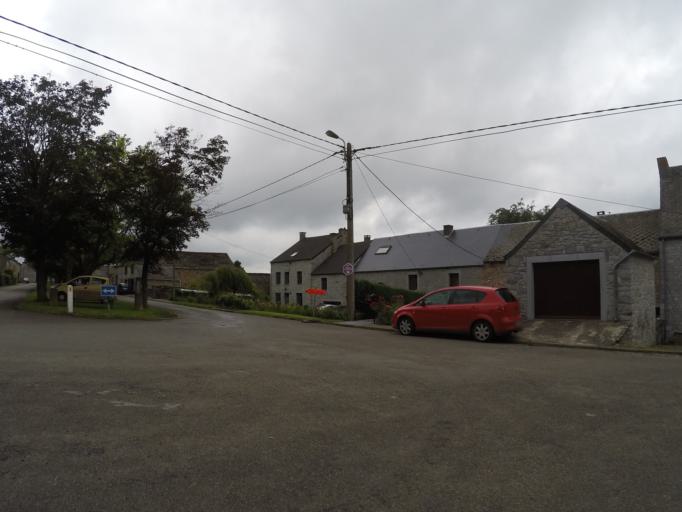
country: BE
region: Wallonia
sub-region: Province de Namur
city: Yvoir
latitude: 50.3218
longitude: 4.9174
